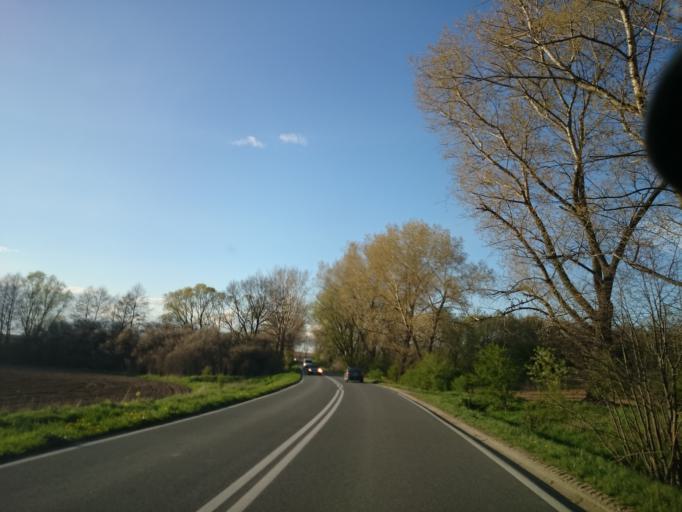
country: PL
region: Lower Silesian Voivodeship
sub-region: Powiat zabkowicki
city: Kamieniec Zabkowicki
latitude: 50.5396
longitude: 16.8647
